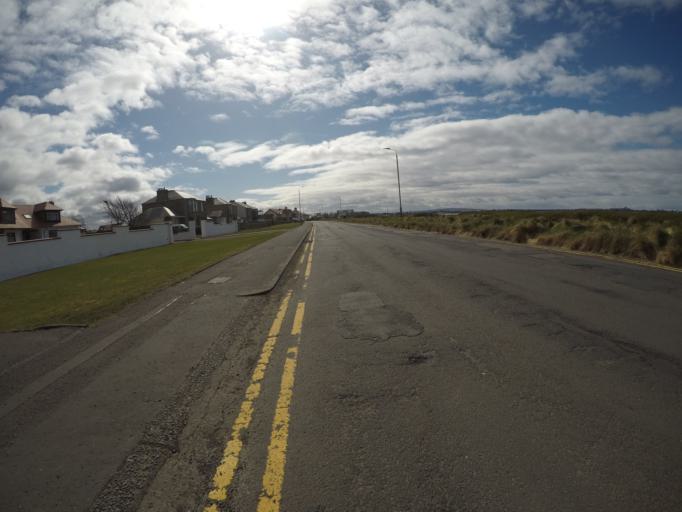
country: GB
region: Scotland
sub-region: South Ayrshire
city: Troon
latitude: 55.5625
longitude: -4.6573
